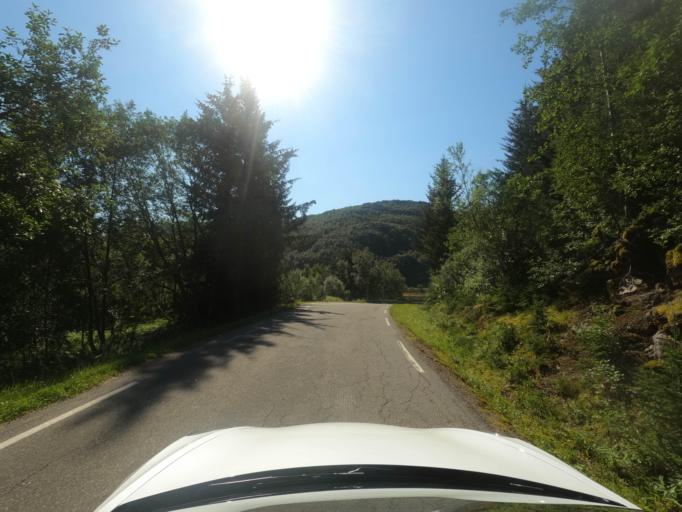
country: NO
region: Nordland
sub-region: Hadsel
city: Stokmarknes
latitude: 68.3023
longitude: 15.0415
